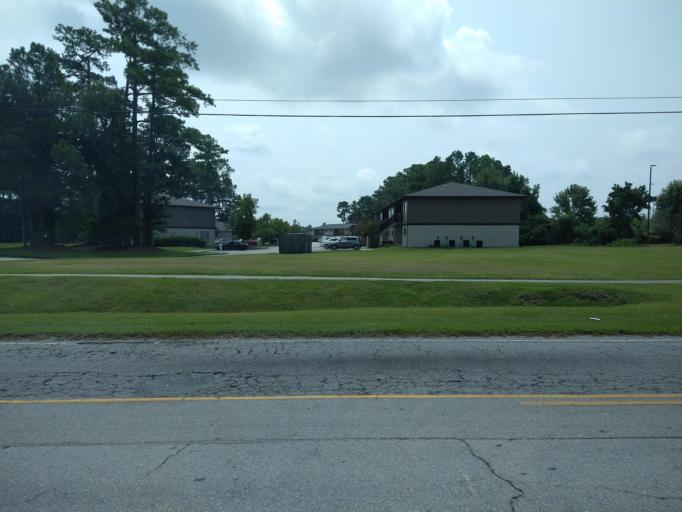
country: US
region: North Carolina
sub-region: Onslow County
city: Pumpkin Center
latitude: 34.7690
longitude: -77.3775
